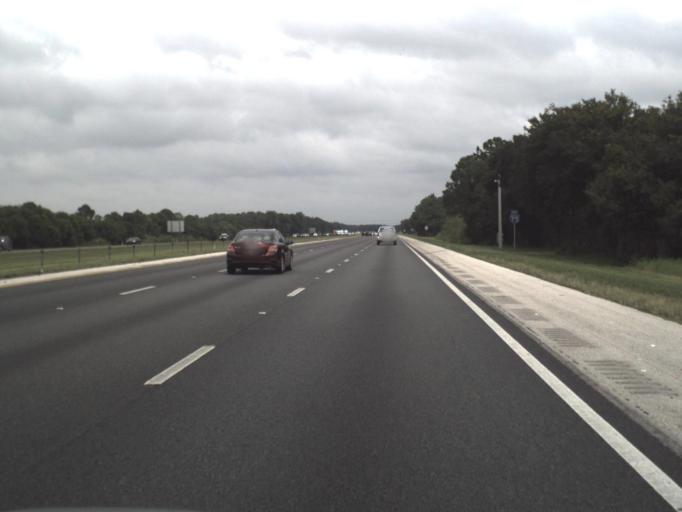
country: US
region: Florida
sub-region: Sarasota County
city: Desoto Lakes
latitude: 27.4488
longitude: -82.4591
